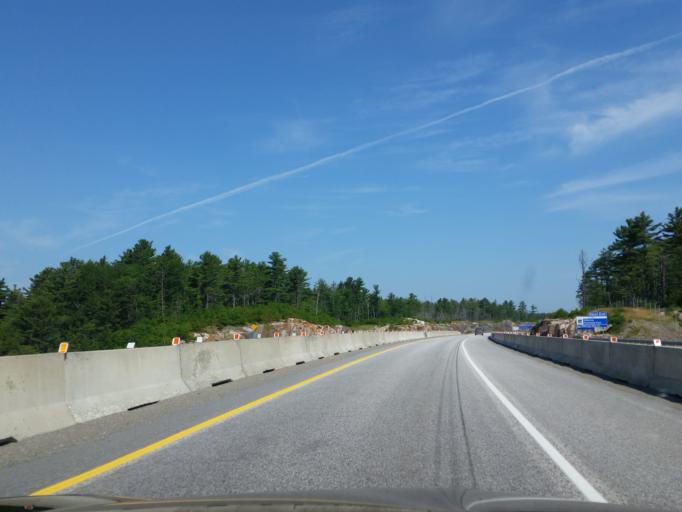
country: CA
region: Ontario
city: Greater Sudbury
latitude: 46.2058
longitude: -80.7645
